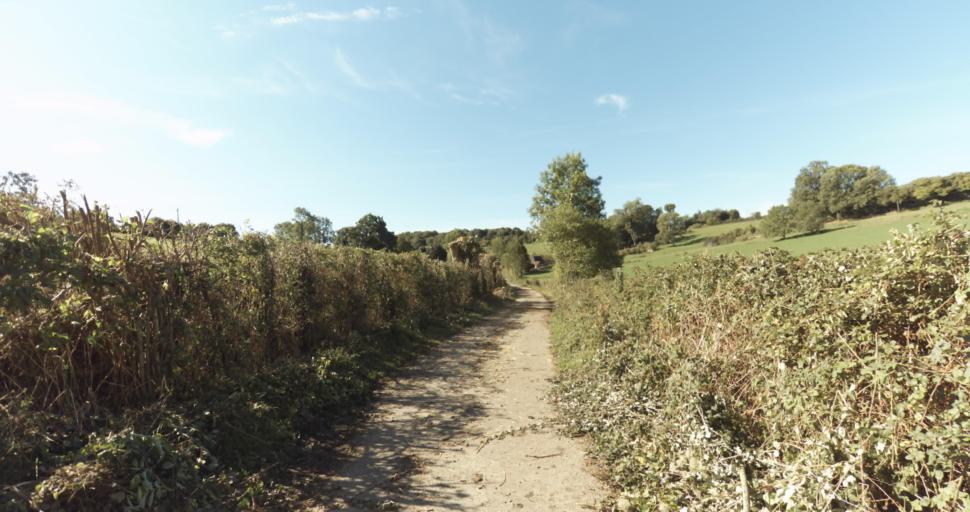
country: FR
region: Lower Normandy
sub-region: Departement de l'Orne
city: Gace
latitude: 48.7993
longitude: 0.2395
